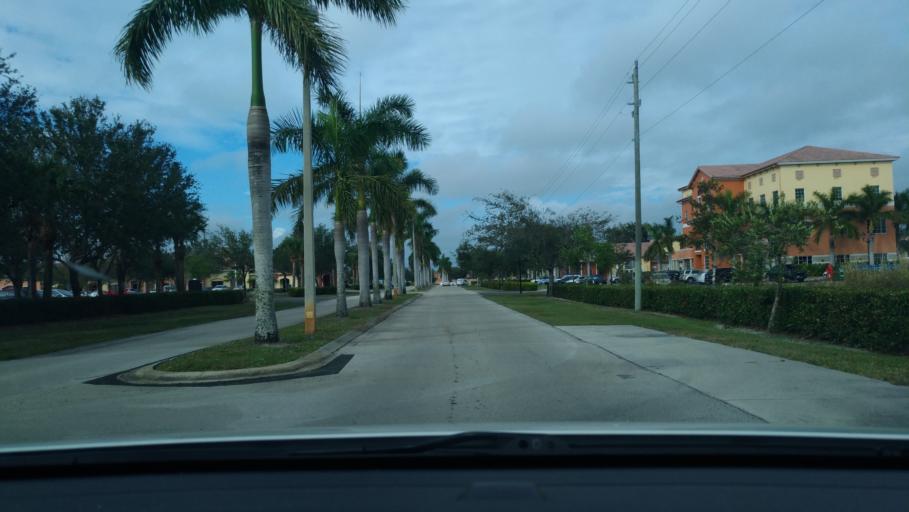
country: US
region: Florida
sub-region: Lee County
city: Estero
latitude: 26.4295
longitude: -81.7997
